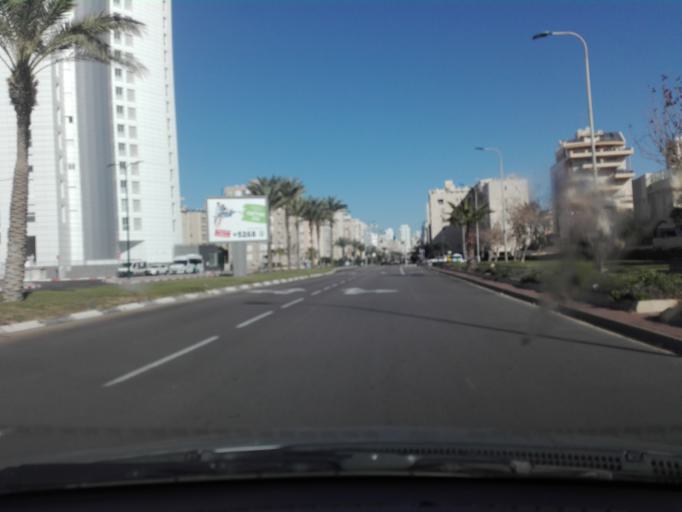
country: IL
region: Central District
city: Netanya
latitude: 32.3184
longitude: 34.8479
